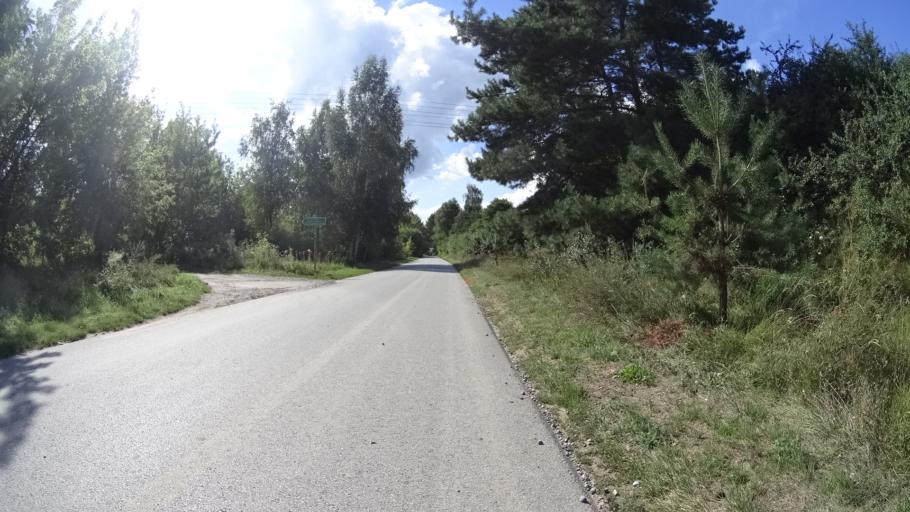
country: PL
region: Masovian Voivodeship
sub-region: Powiat grojecki
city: Mogielnica
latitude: 51.6942
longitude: 20.7130
